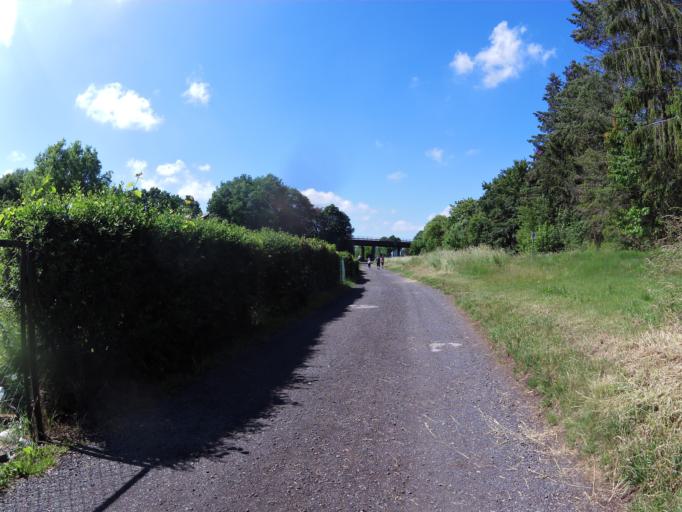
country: DE
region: Hesse
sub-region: Regierungsbezirk Kassel
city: Bad Hersfeld
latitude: 50.8567
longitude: 9.6931
